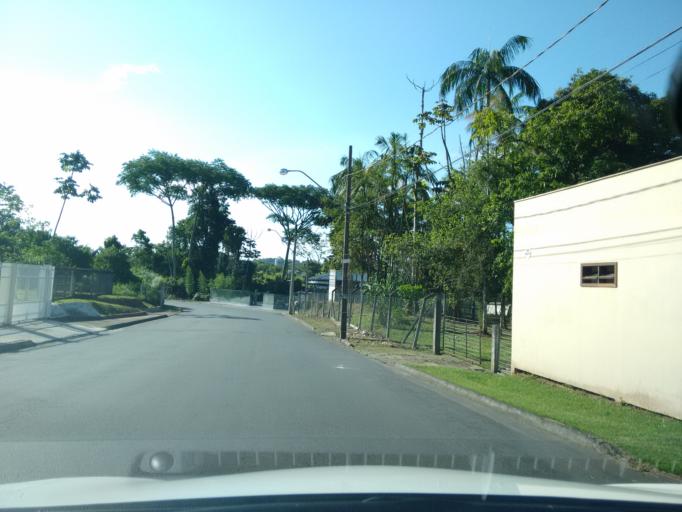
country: BR
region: Santa Catarina
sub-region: Blumenau
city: Blumenau
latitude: -26.8974
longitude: -49.0655
